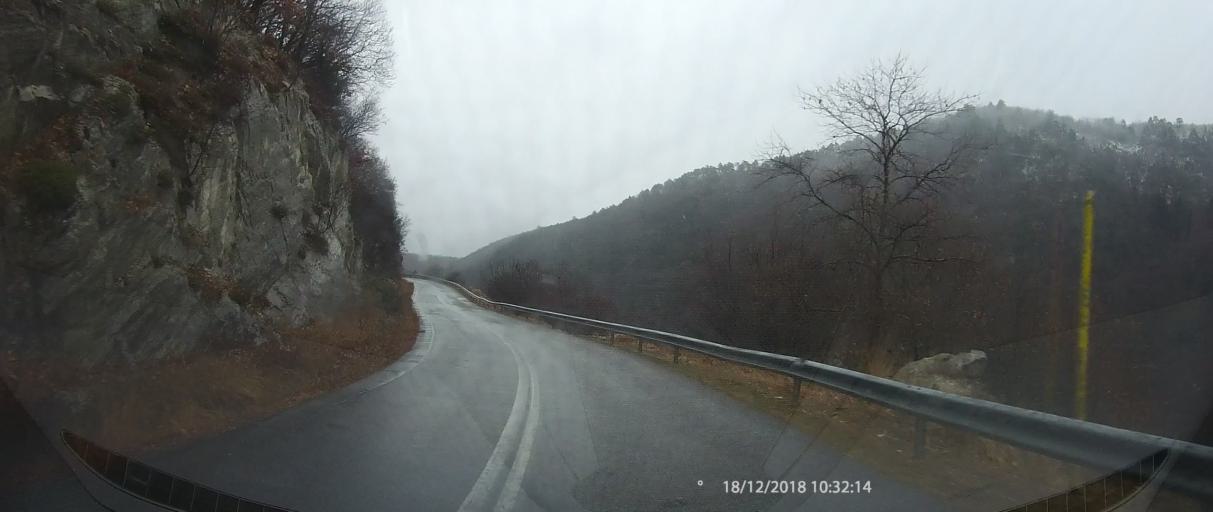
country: GR
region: Central Macedonia
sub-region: Nomos Pierias
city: Kato Milia
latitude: 40.1909
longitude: 22.2900
